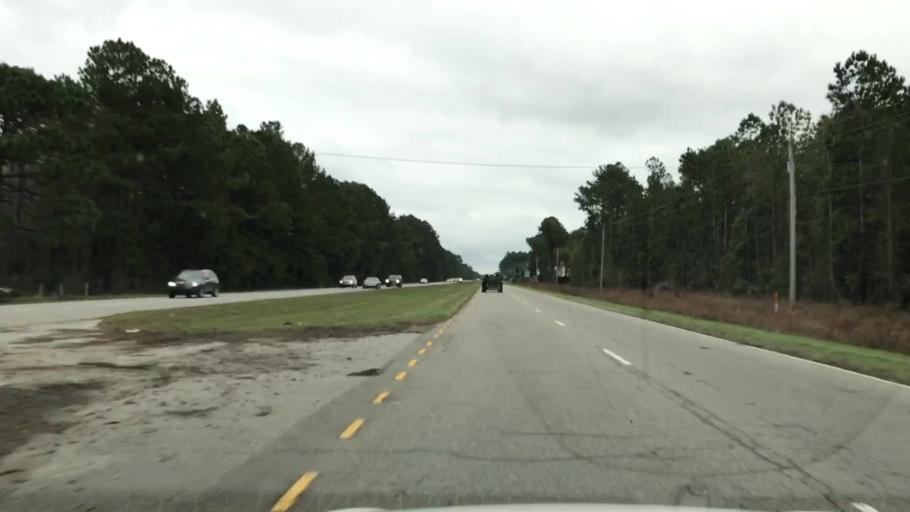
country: US
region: South Carolina
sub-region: Georgetown County
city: Georgetown
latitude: 33.3056
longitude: -79.3362
